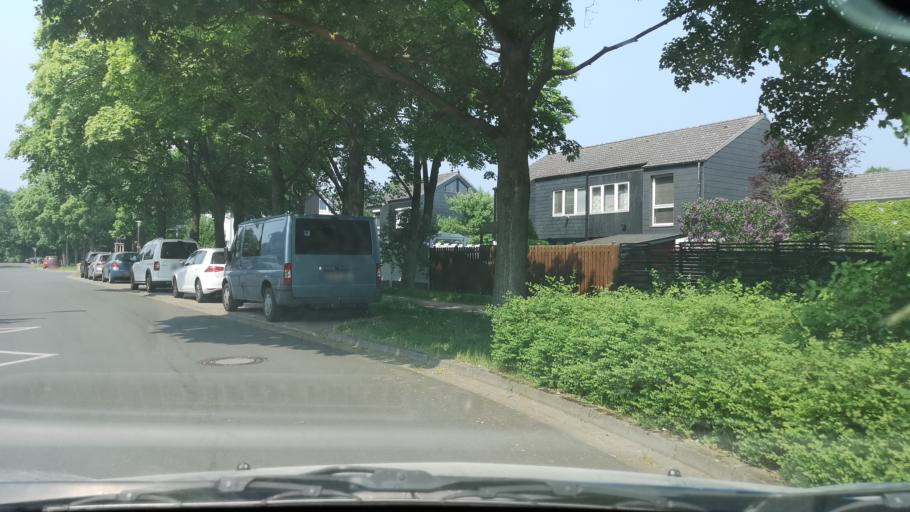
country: DE
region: Lower Saxony
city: Langenhagen
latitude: 52.4441
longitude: 9.7560
